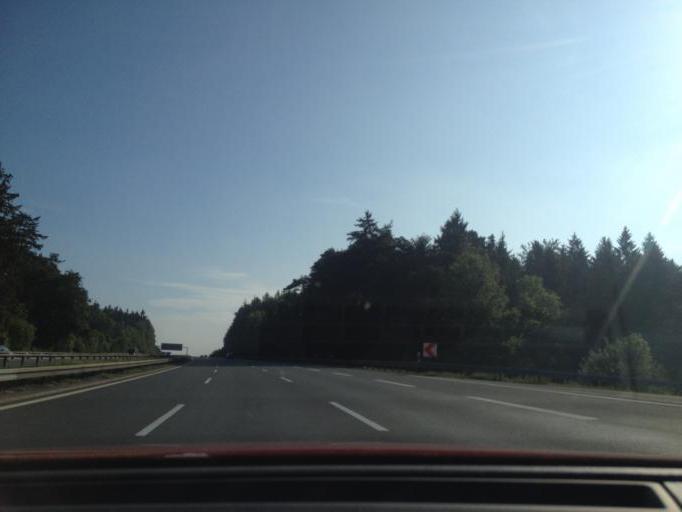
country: DE
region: Bavaria
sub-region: Regierungsbezirk Mittelfranken
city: Kirchensittenbach
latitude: 49.6217
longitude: 11.4098
